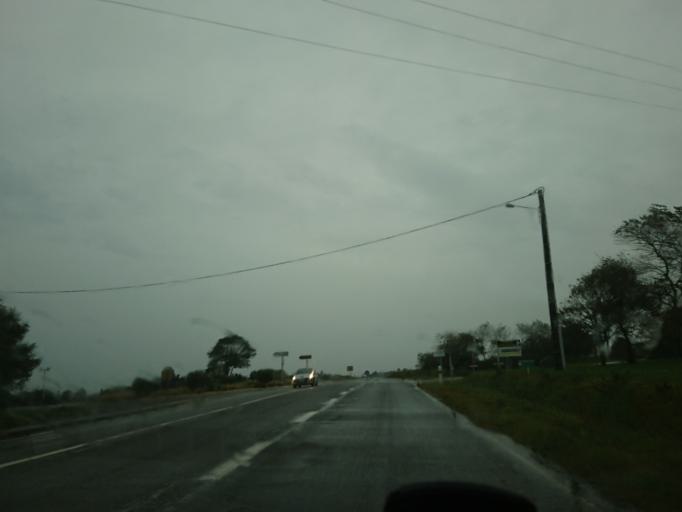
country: FR
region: Brittany
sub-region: Departement du Finistere
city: Plouguerneau
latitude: 48.6076
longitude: -4.4973
